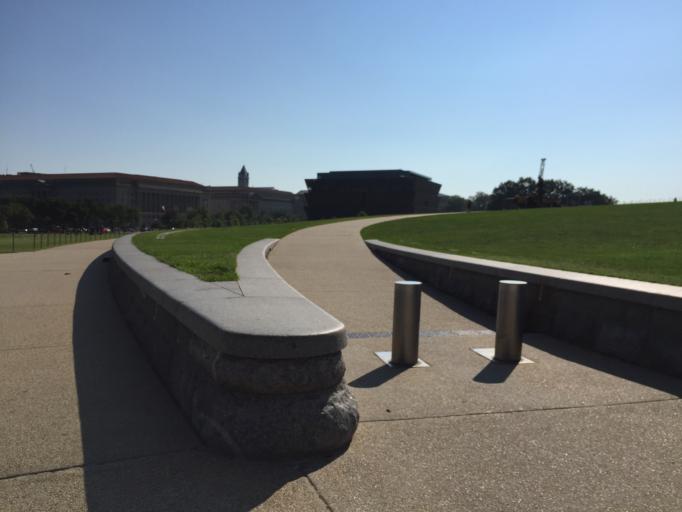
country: US
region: Washington, D.C.
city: Washington, D.C.
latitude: 38.8900
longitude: -77.0367
